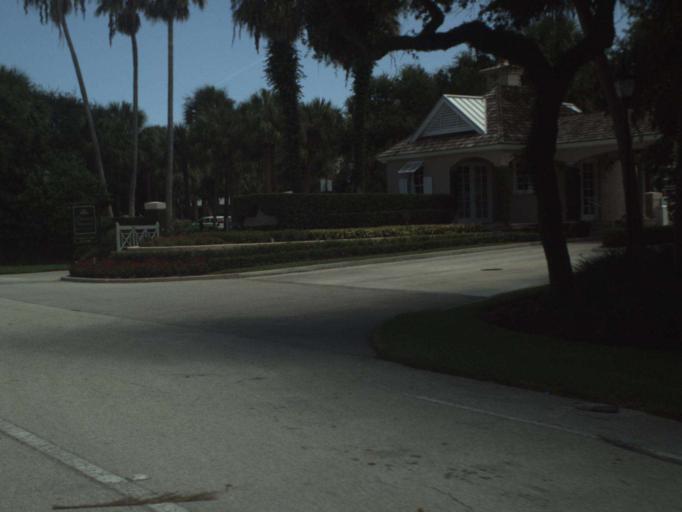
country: US
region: Florida
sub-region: Indian River County
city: Wabasso Beach
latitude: 27.7732
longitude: -80.4034
